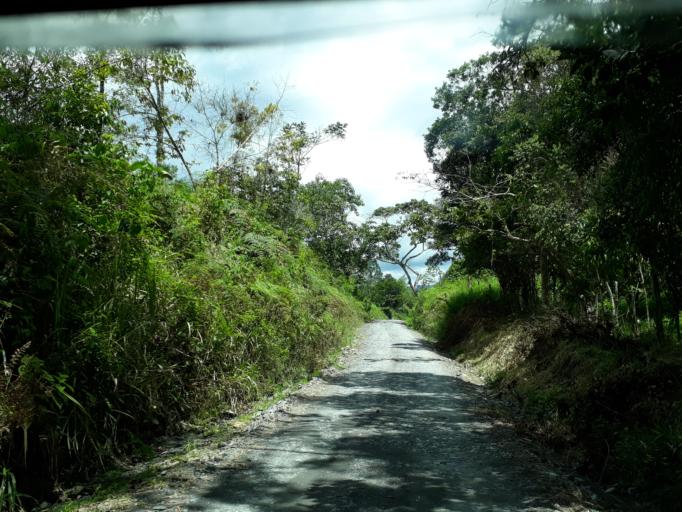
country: CO
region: Cundinamarca
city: Topaipi
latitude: 5.3636
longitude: -74.1977
